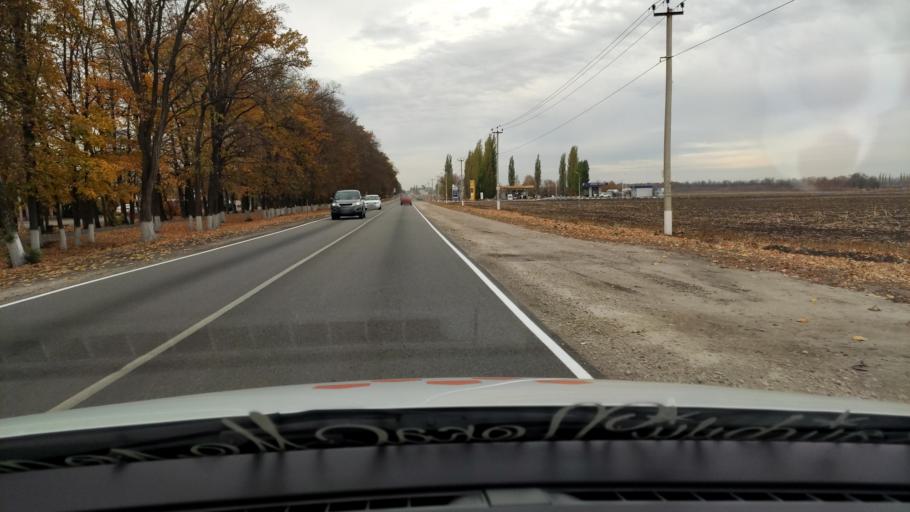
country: RU
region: Voronezj
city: Ramon'
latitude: 51.9114
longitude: 39.3263
